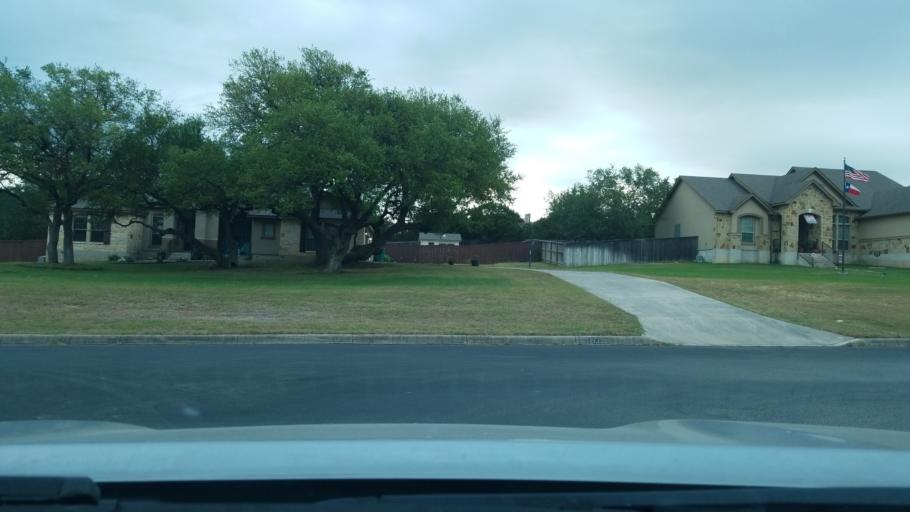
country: US
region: Texas
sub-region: Bexar County
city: Timberwood Park
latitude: 29.7110
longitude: -98.4948
